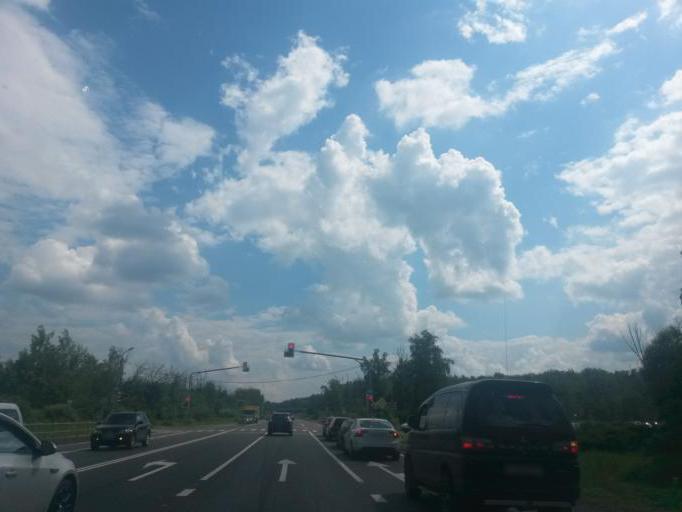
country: RU
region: Moskovskaya
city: Vostryakovo
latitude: 55.3699
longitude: 37.7867
